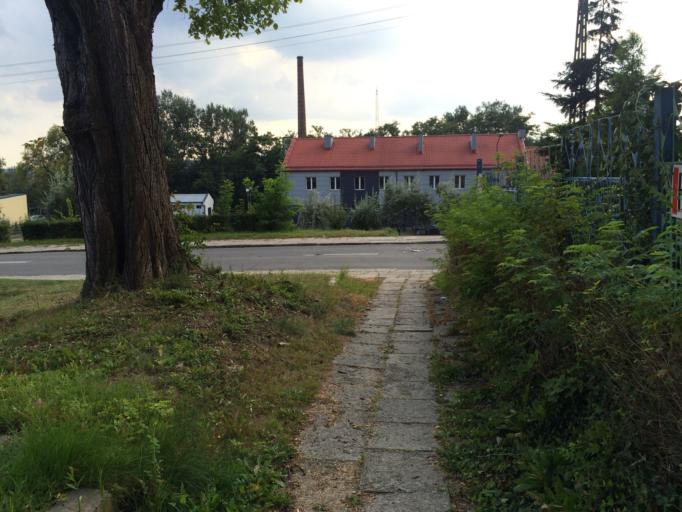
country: PL
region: Swietokrzyskie
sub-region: Powiat starachowicki
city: Starachowice
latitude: 51.0507
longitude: 21.0669
